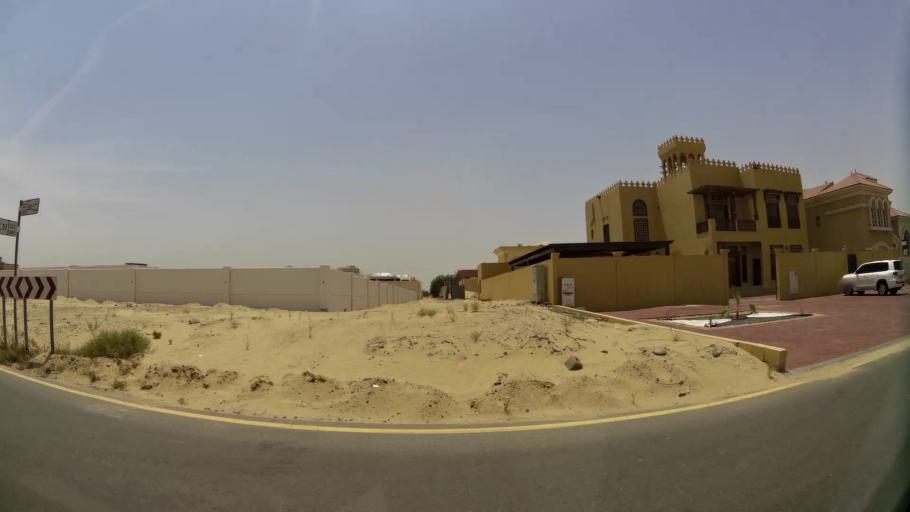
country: AE
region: Ash Shariqah
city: Sharjah
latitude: 25.2403
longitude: 55.4882
